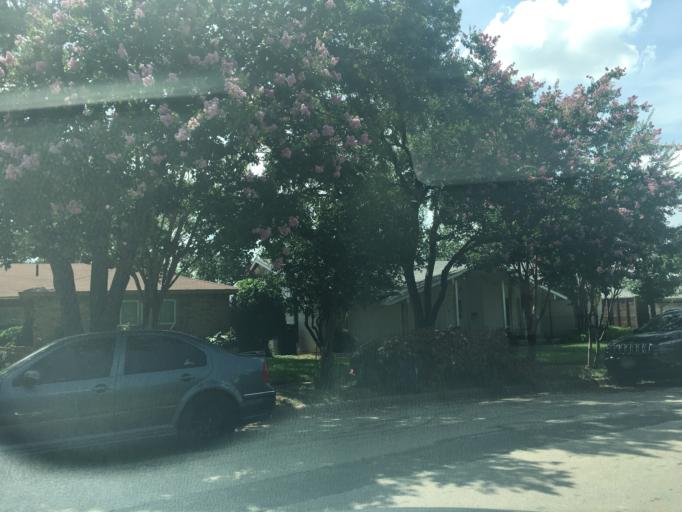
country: US
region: Texas
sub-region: Dallas County
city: Farmers Branch
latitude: 32.9139
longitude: -96.8537
